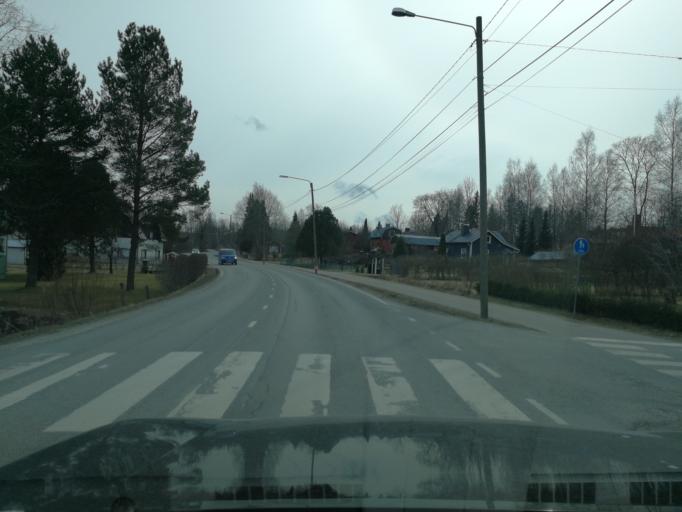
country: FI
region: Uusimaa
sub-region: Helsinki
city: Lohja
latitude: 60.1978
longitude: 24.0032
